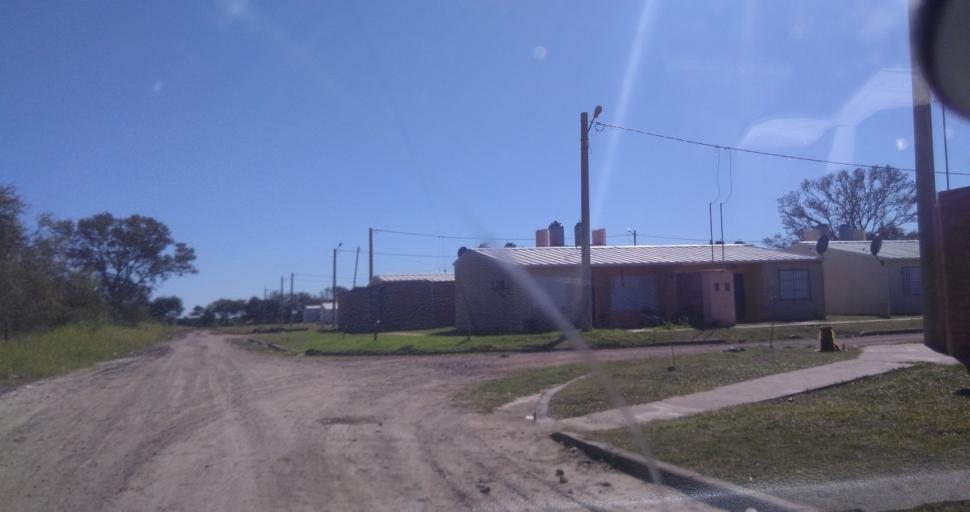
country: AR
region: Chaco
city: Fontana
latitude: -27.4578
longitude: -59.0504
